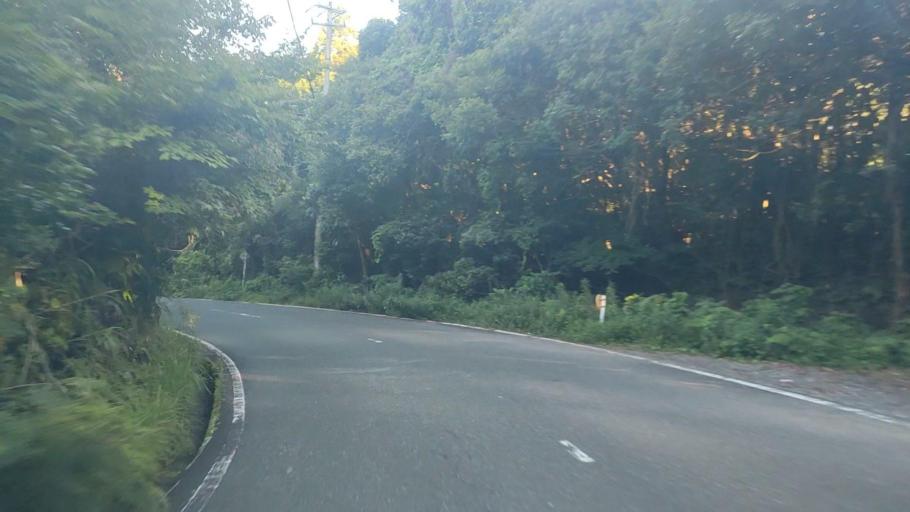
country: JP
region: Mie
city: Toba
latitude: 34.2642
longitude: 136.7714
